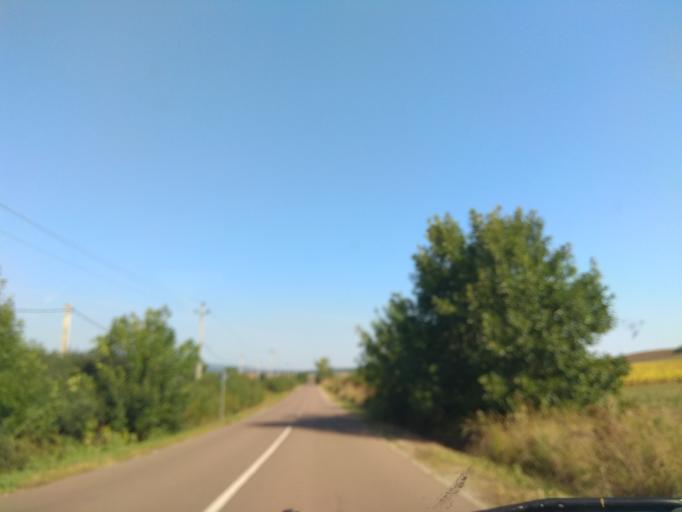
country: HU
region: Borsod-Abauj-Zemplen
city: Nyekladhaza
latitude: 47.9678
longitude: 20.7993
